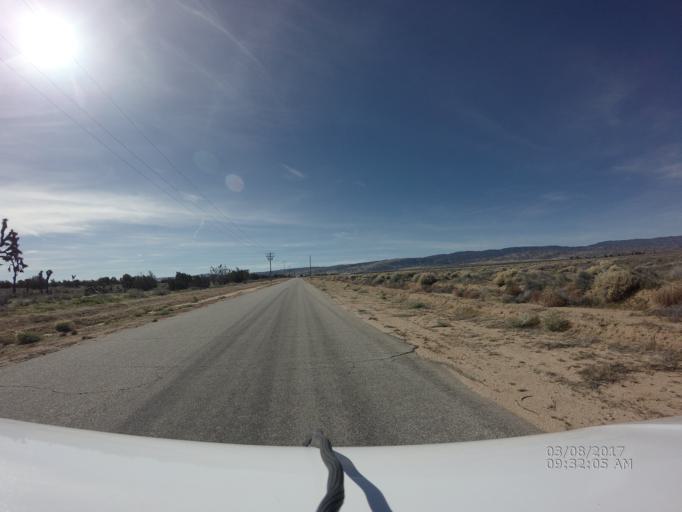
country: US
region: California
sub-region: Los Angeles County
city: Green Valley
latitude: 34.7807
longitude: -118.4666
